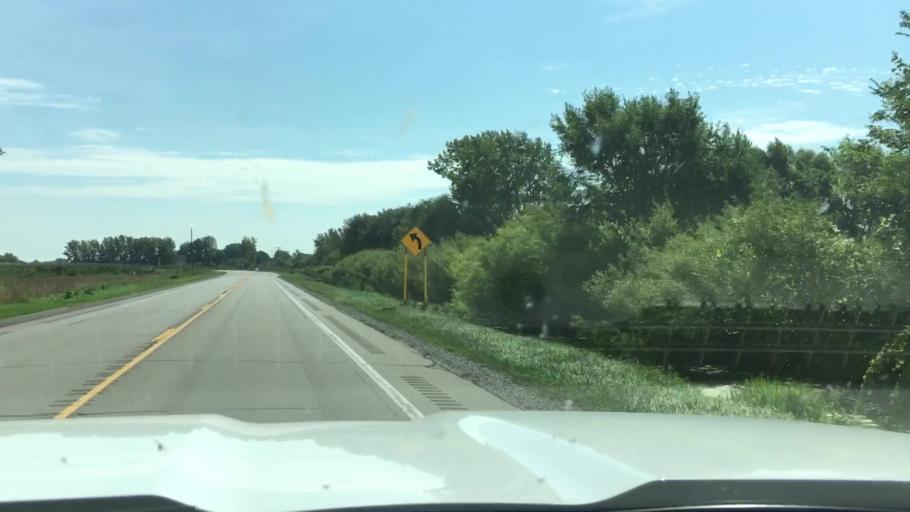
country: US
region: Michigan
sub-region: Tuscola County
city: Reese
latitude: 43.5807
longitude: -83.7019
